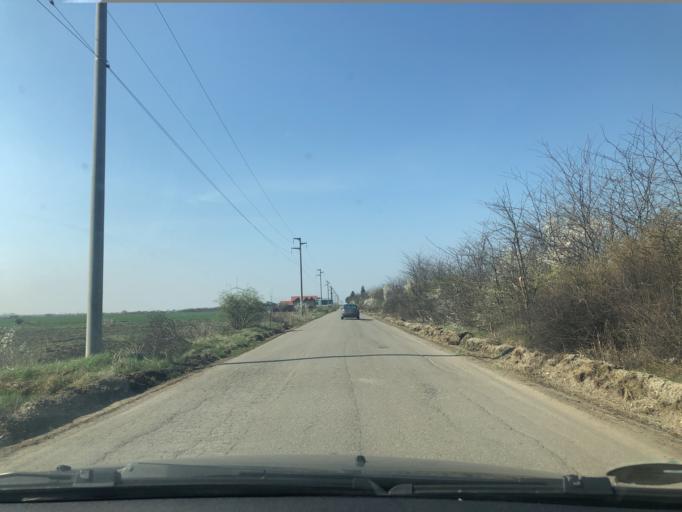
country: RO
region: Ilfov
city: Domnesti-Sarbi
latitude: 44.3693
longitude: 25.9201
